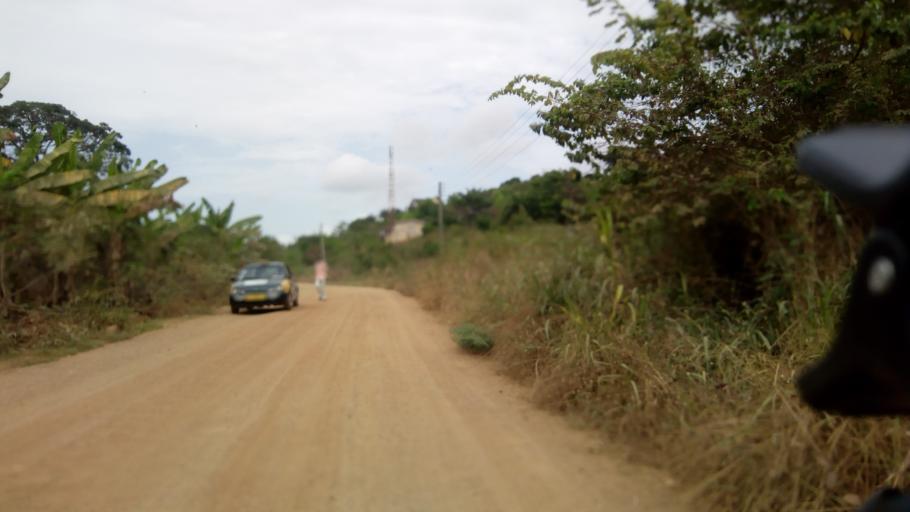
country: GH
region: Central
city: Cape Coast
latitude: 5.1077
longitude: -1.2731
